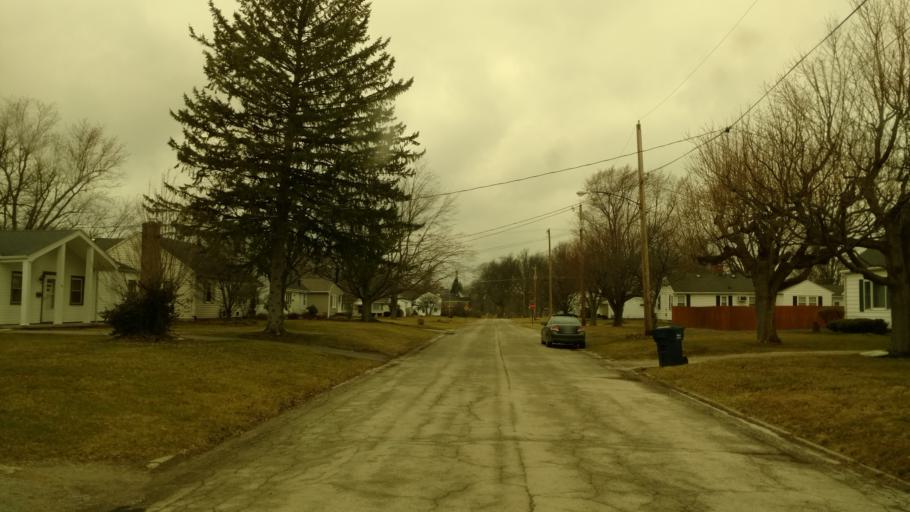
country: US
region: Ohio
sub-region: Richland County
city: Shelby
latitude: 40.8797
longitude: -82.6447
